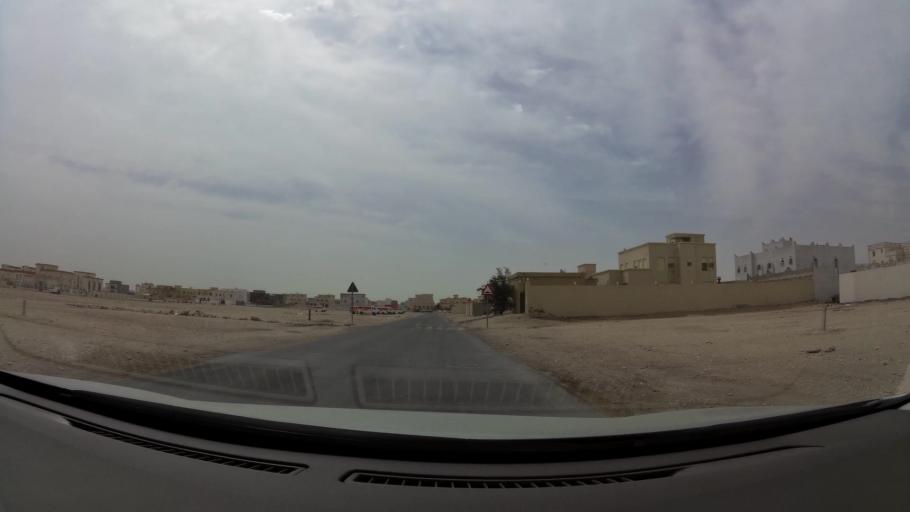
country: QA
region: Baladiyat ar Rayyan
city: Ar Rayyan
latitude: 25.2099
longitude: 51.4517
